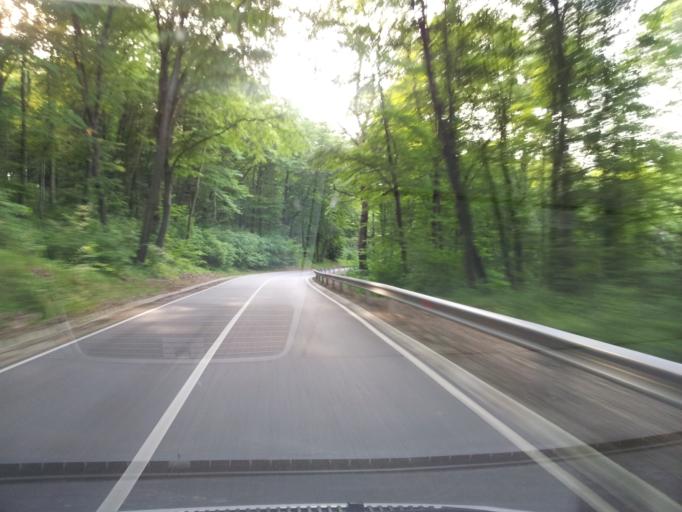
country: HU
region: Komarom-Esztergom
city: Kesztolc
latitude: 47.7324
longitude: 18.8281
